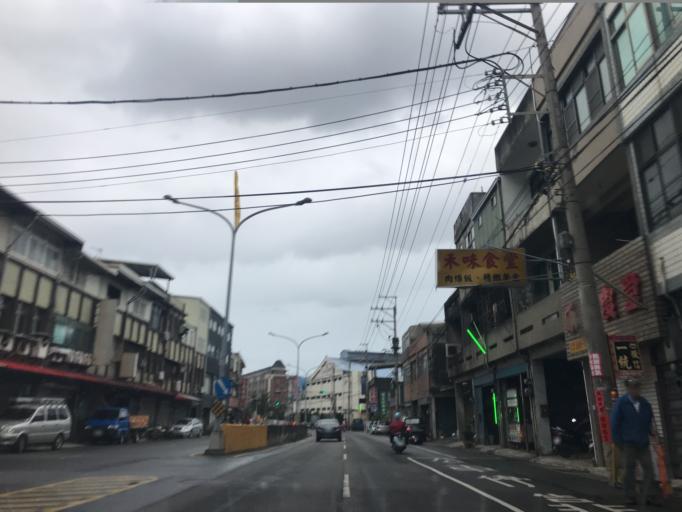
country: TW
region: Taiwan
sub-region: Hsinchu
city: Zhubei
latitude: 24.8335
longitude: 121.0285
